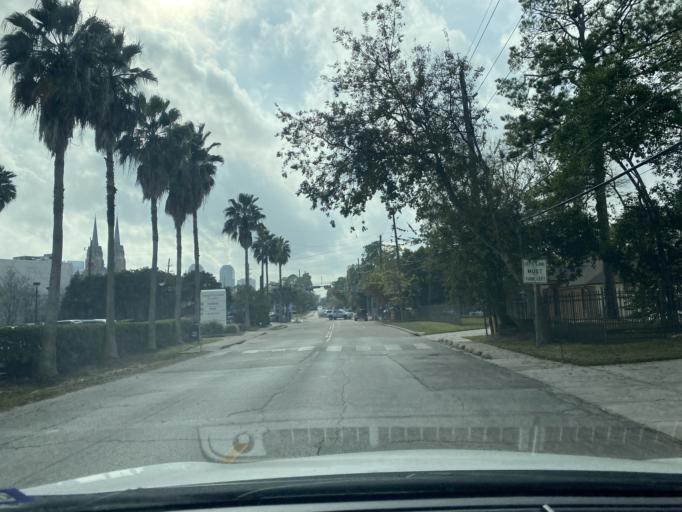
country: US
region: Texas
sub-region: Harris County
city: Hunters Creek Village
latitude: 29.7639
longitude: -95.4677
